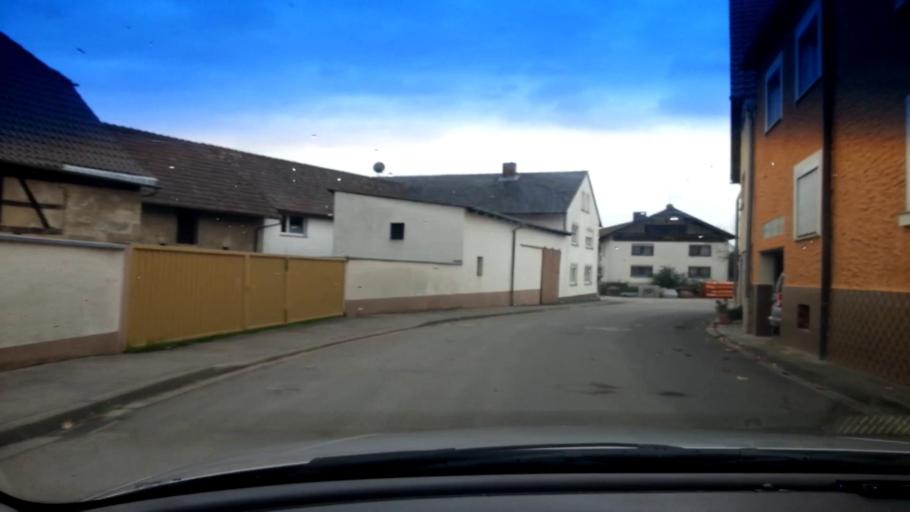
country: DE
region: Bavaria
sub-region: Regierungsbezirk Unterfranken
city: Stettfeld
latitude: 49.9721
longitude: 10.7258
